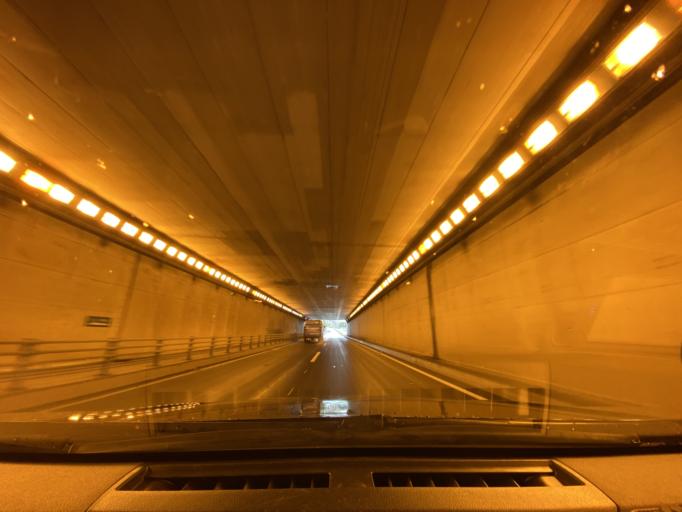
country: JP
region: Hokkaido
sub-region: Asahikawa-shi
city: Asahikawa
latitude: 43.8085
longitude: 142.3589
